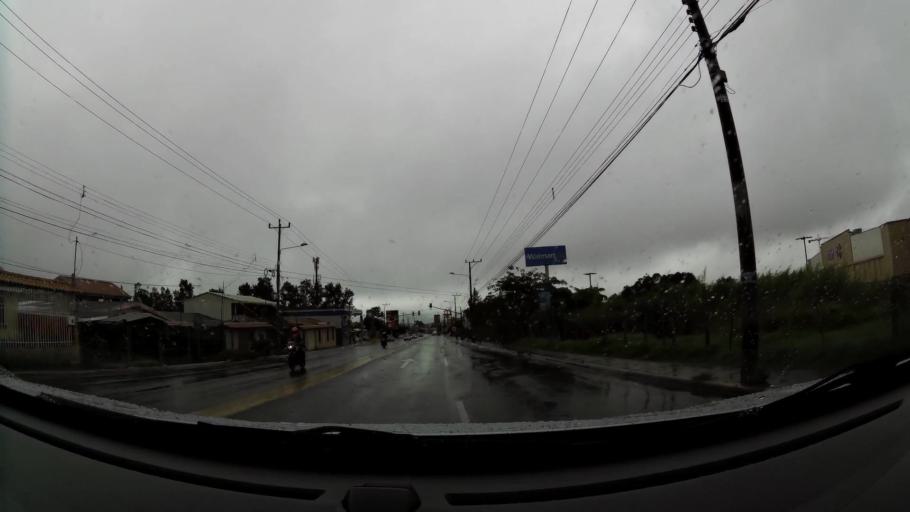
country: CR
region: Cartago
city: Cartago
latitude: 9.8580
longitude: -83.9054
